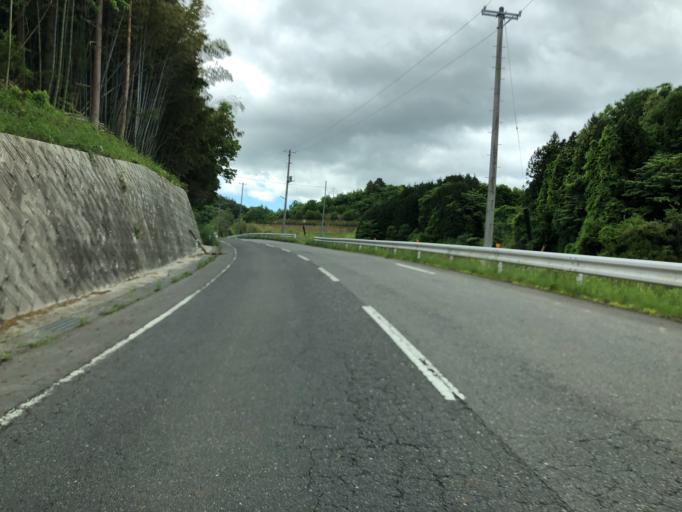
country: JP
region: Fukushima
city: Nihommatsu
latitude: 37.5306
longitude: 140.4589
